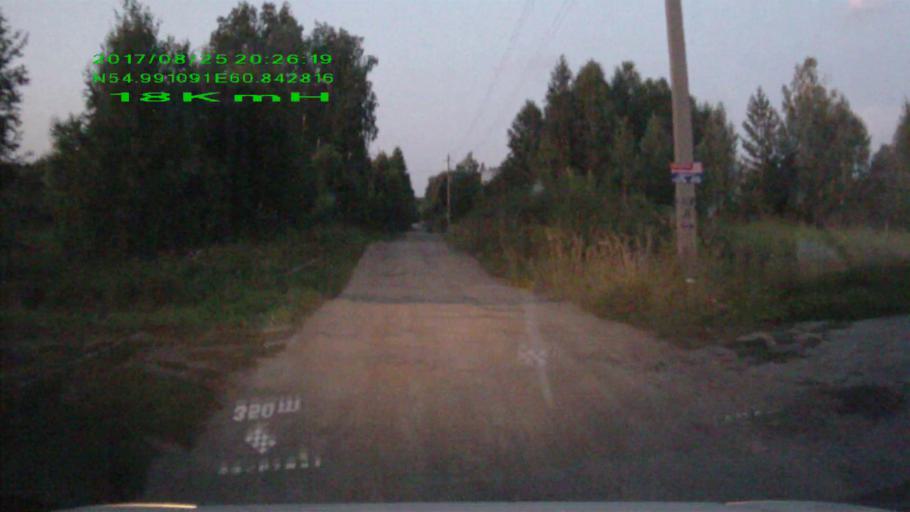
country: RU
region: Chelyabinsk
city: Timiryazevskiy
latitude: 54.9911
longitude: 60.8429
